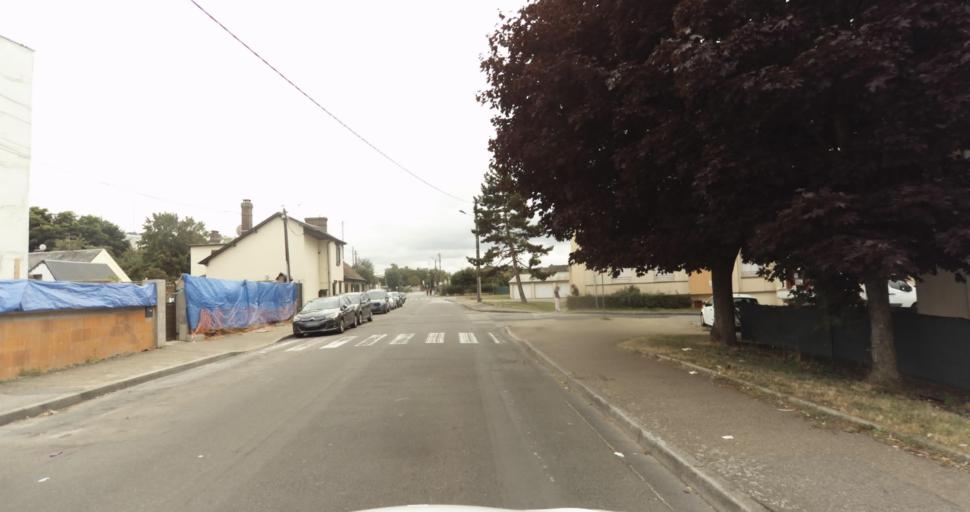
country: FR
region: Haute-Normandie
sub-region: Departement de l'Eure
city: Evreux
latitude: 49.0122
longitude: 1.1605
